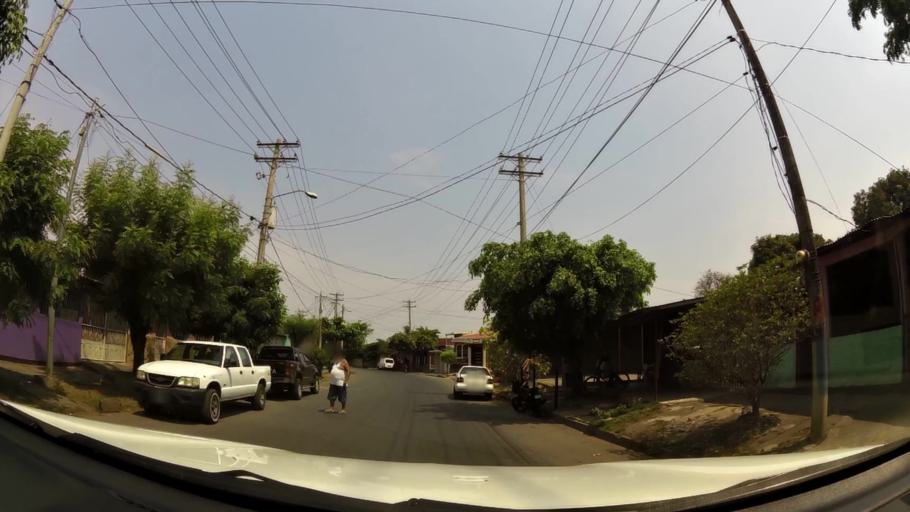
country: NI
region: Managua
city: Ciudad Sandino
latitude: 12.1586
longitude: -86.3049
